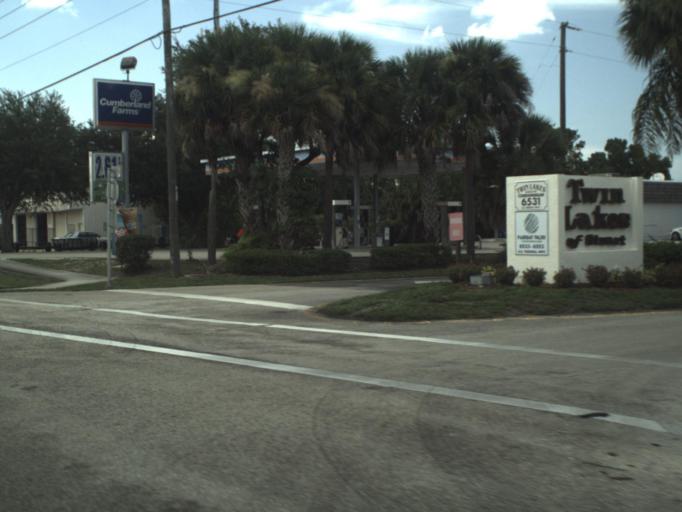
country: US
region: Florida
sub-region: Martin County
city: Port Salerno
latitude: 27.1251
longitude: -80.1924
